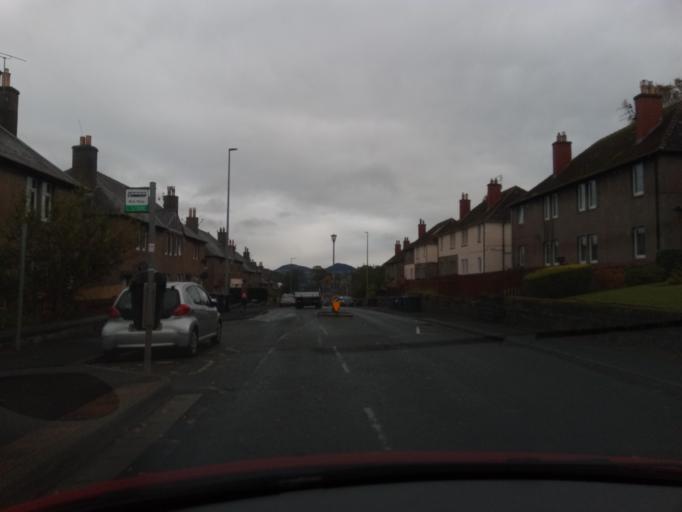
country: GB
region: Scotland
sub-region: The Scottish Borders
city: Galashiels
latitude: 55.6258
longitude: -2.8315
